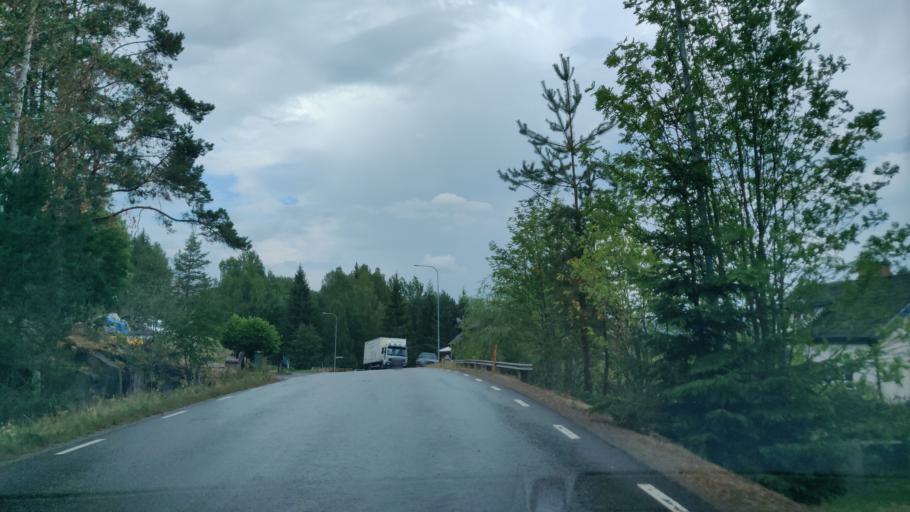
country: SE
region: Vaermland
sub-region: Munkfors Kommun
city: Munkfors
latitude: 59.8438
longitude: 13.5320
